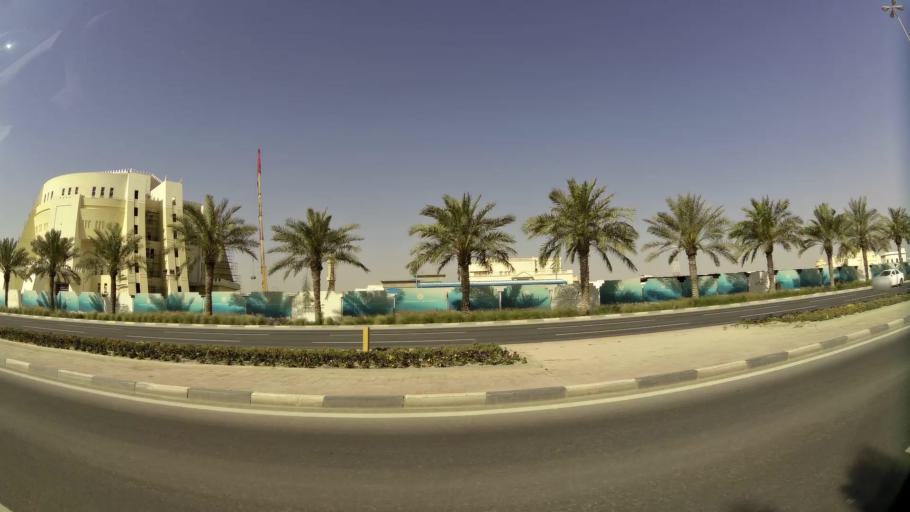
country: QA
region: Baladiyat ad Dawhah
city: Doha
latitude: 25.3086
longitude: 51.5048
